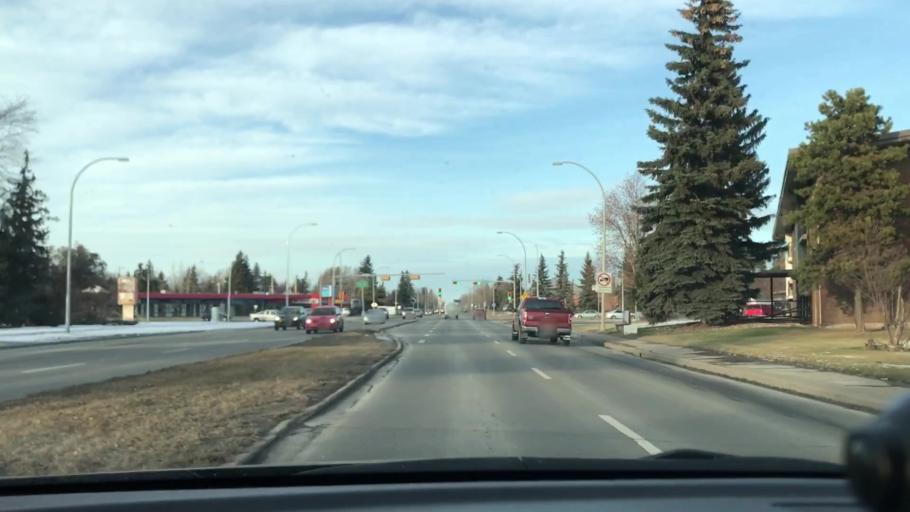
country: CA
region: Alberta
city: Edmonton
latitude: 53.5241
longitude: -113.4429
